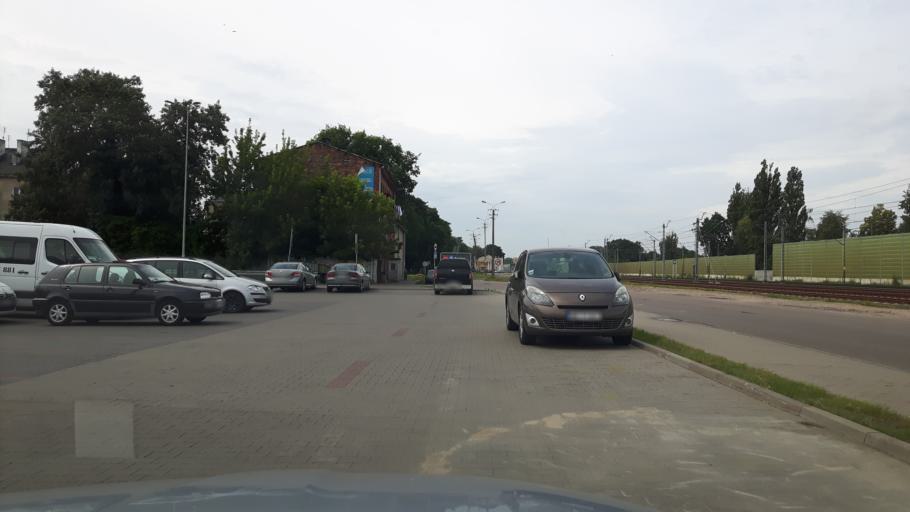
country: PL
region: Masovian Voivodeship
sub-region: Powiat wolominski
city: Wolomin
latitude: 52.3487
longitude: 21.2439
